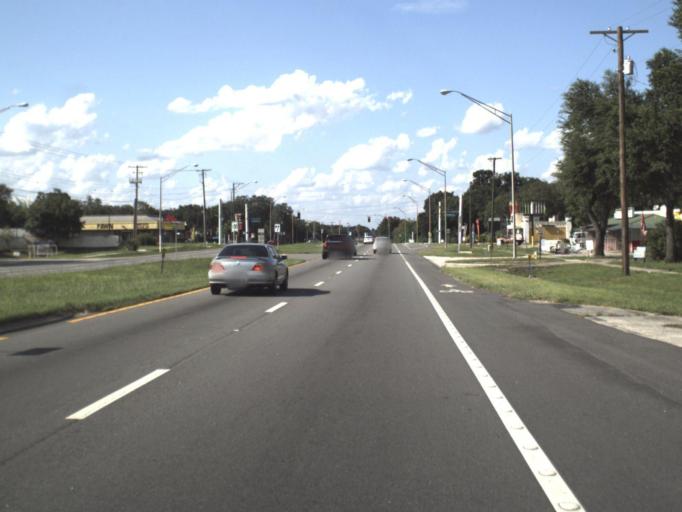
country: US
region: Florida
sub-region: Hillsborough County
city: Temple Terrace
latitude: 28.0182
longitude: -82.3933
